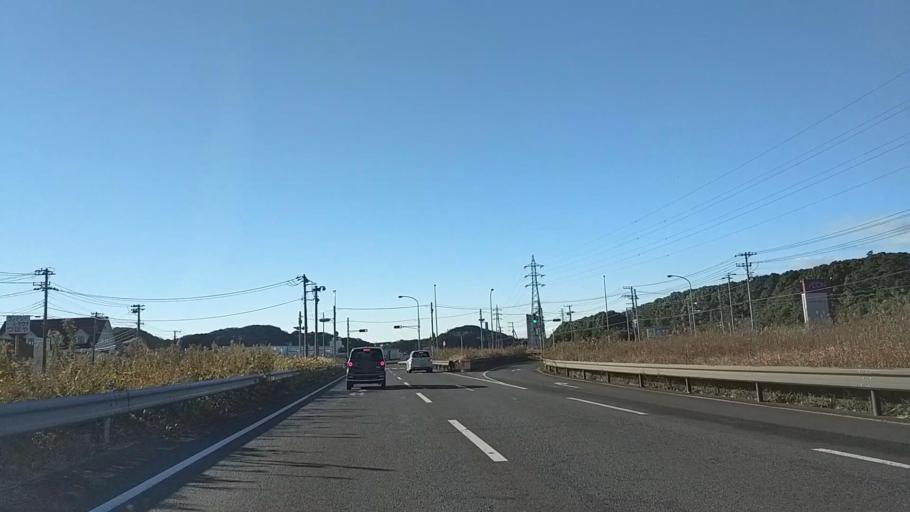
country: JP
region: Chiba
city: Kisarazu
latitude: 35.3637
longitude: 139.9116
